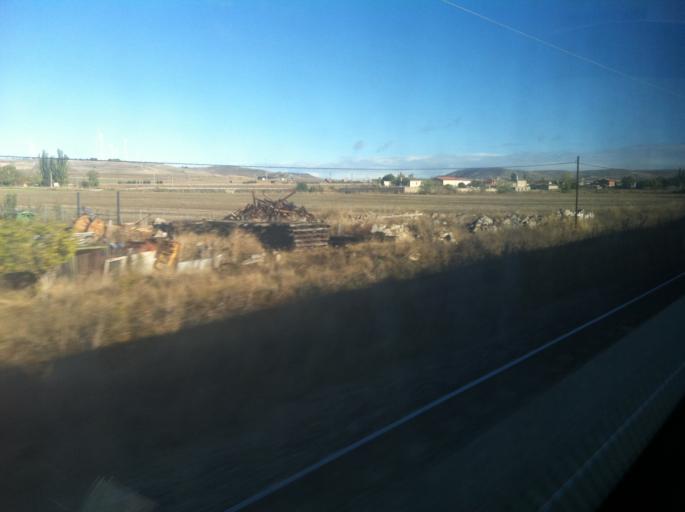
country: ES
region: Castille and Leon
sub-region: Provincia de Burgos
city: Villaquiran de los Infantes
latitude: 42.2200
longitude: -3.9949
